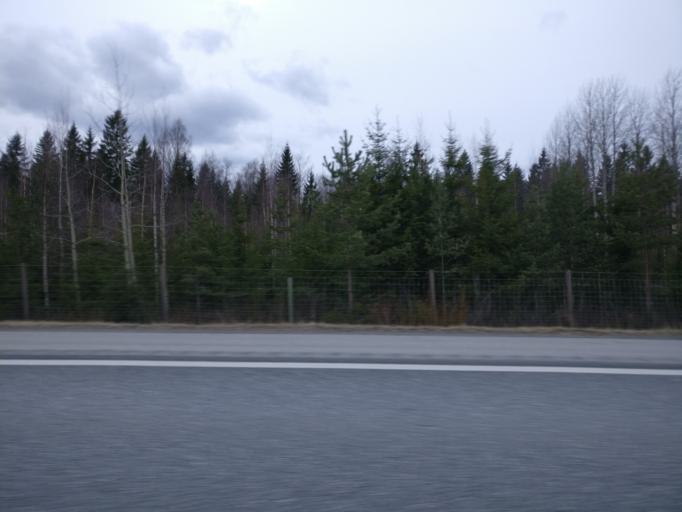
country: FI
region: Haeme
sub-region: Haemeenlinna
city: Tervakoski
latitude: 60.8049
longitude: 24.6814
